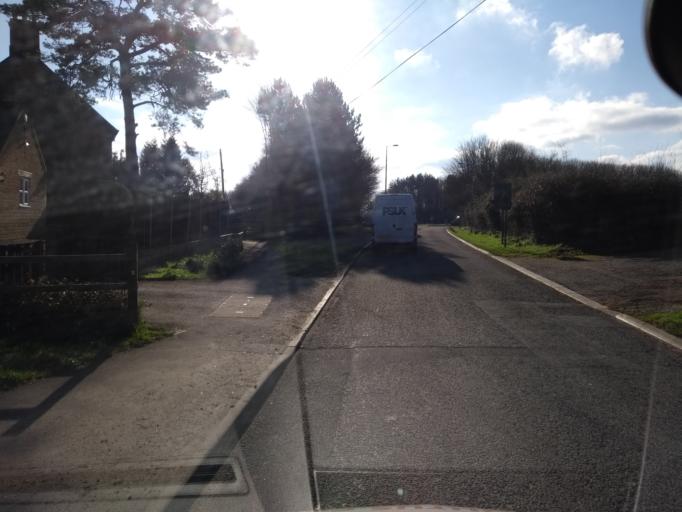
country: GB
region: England
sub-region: Somerset
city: South Petherton
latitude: 50.9435
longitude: -2.8027
